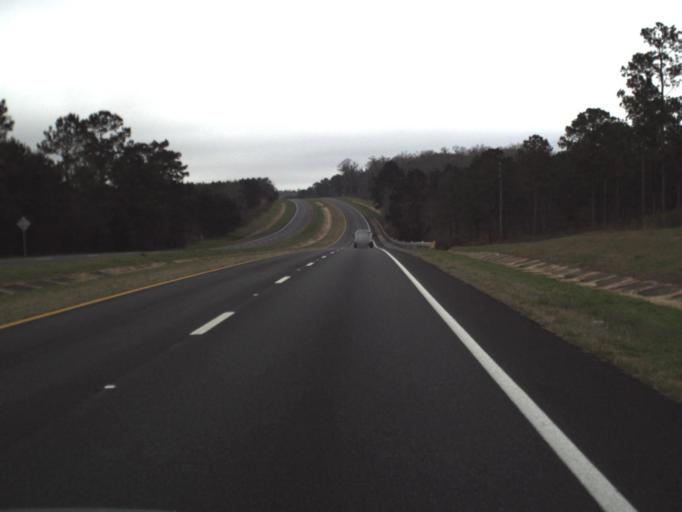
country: US
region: Florida
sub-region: Jefferson County
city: Monticello
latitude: 30.4002
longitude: -83.8808
